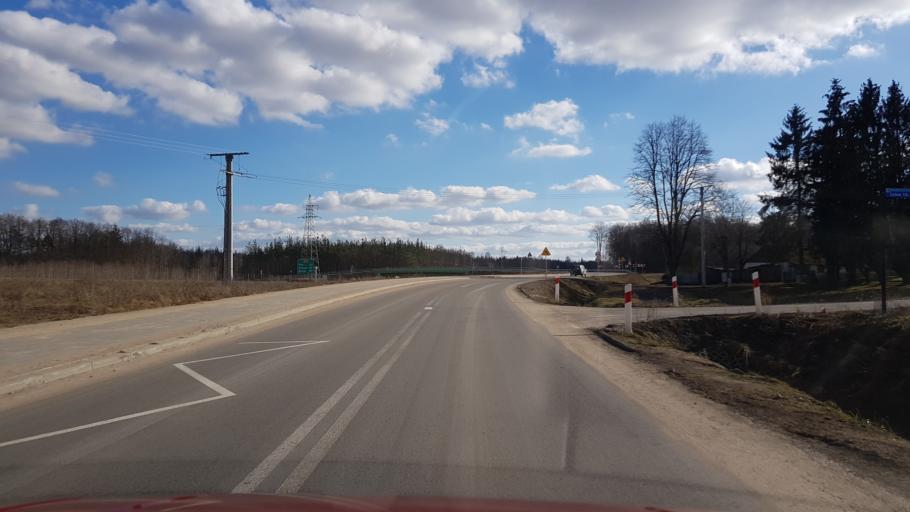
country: PL
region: West Pomeranian Voivodeship
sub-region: Powiat szczecinecki
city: Szczecinek
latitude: 53.6858
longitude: 16.7322
